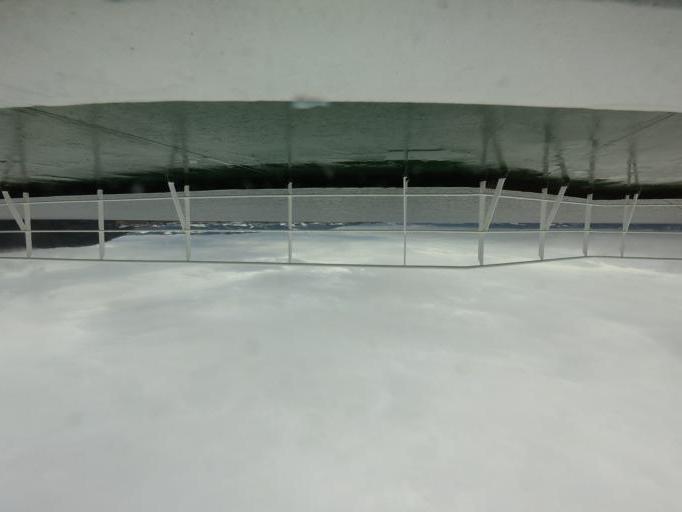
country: NO
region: Sor-Trondelag
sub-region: Skaun
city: Borsa
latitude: 63.4750
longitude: 10.0630
